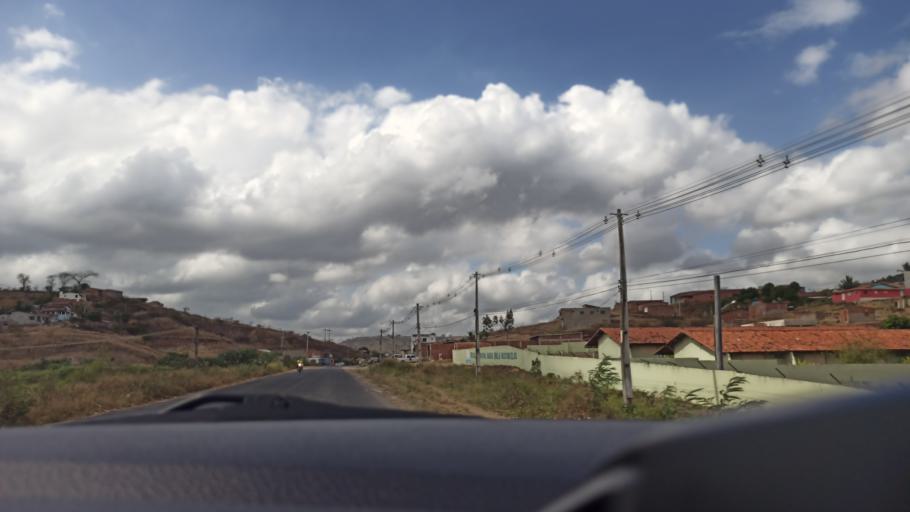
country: BR
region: Pernambuco
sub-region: Timbauba
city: Timbauba
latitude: -7.5020
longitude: -35.2989
